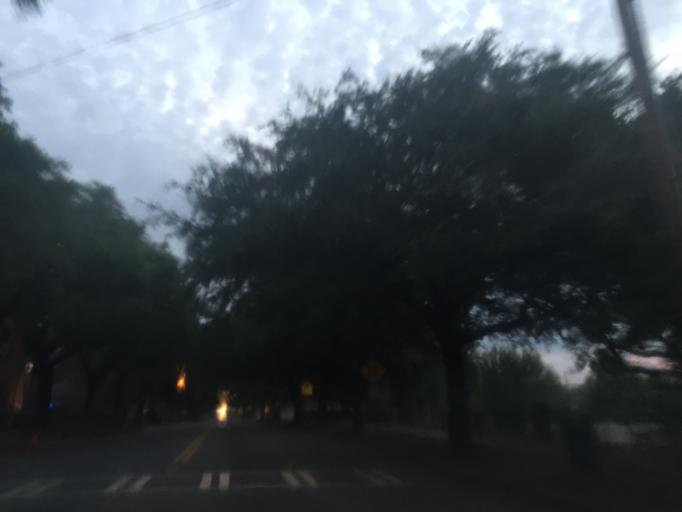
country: US
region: Georgia
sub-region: Chatham County
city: Savannah
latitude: 32.0685
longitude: -81.0879
